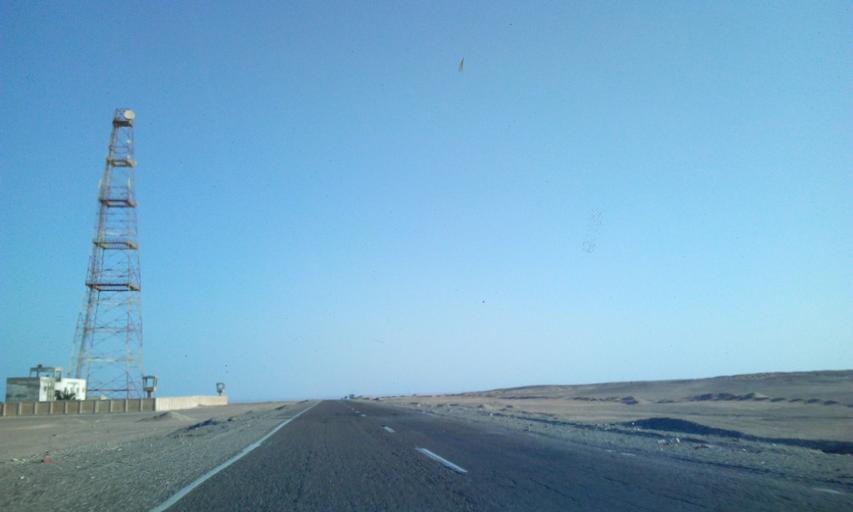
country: EG
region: South Sinai
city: Tor
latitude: 28.6869
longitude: 32.8316
